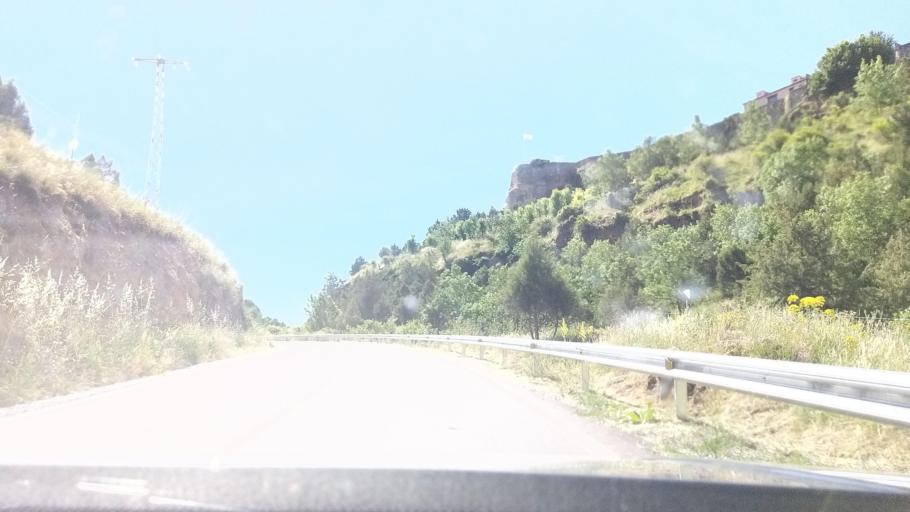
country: ES
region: Castille and Leon
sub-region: Provincia de Segovia
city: Pedraza
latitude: 41.1334
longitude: -3.8125
